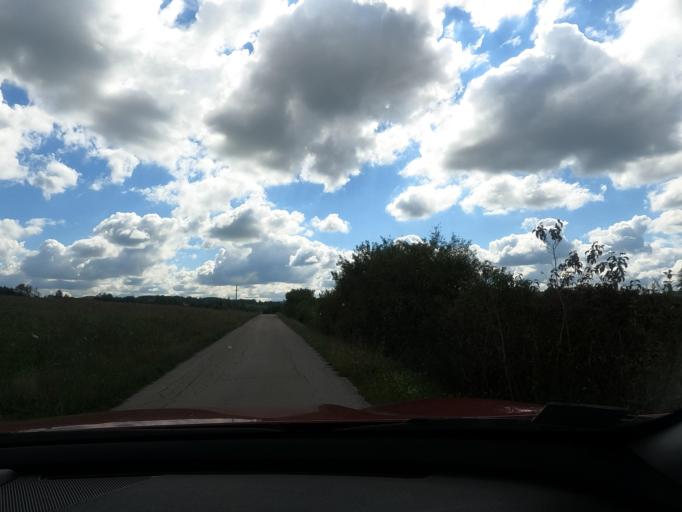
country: BA
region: Federation of Bosnia and Herzegovina
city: Velika Kladusa
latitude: 45.2173
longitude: 15.7117
